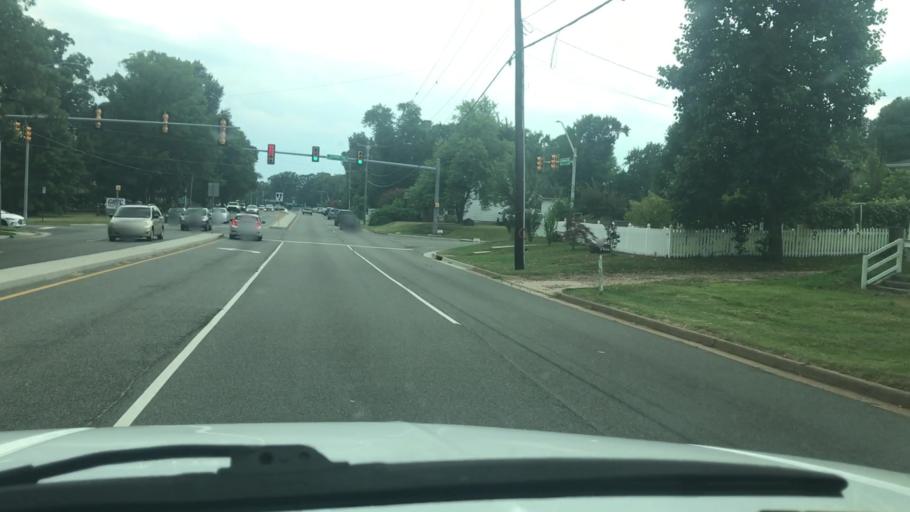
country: US
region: Virginia
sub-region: Henrico County
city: Tuckahoe
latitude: 37.6213
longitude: -77.5574
